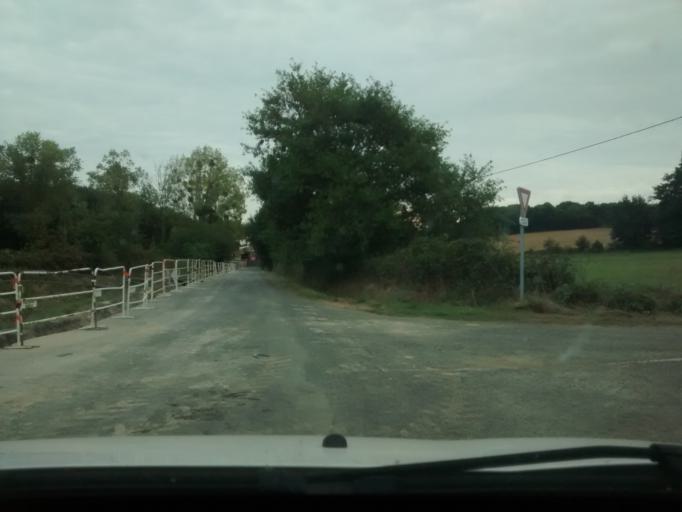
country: FR
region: Brittany
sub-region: Departement d'Ille-et-Vilaine
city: Cesson-Sevigne
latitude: 48.1005
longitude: -1.5914
